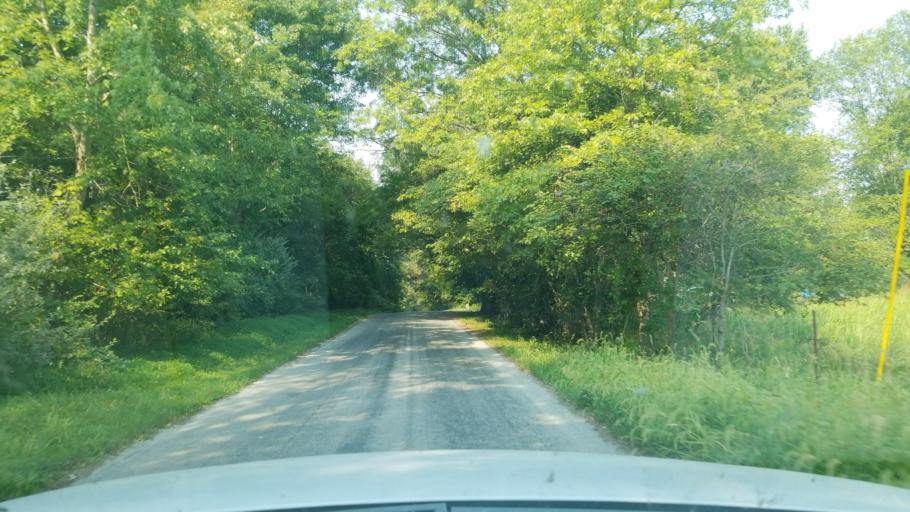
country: US
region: Illinois
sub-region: Saline County
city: Carrier Mills
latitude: 37.7905
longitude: -88.6794
